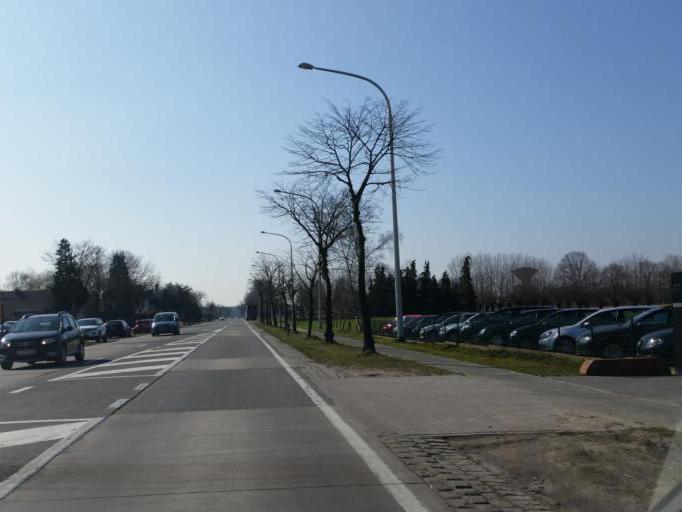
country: BE
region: Flanders
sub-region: Provincie Oost-Vlaanderen
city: Lokeren
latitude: 51.1232
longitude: 4.0306
